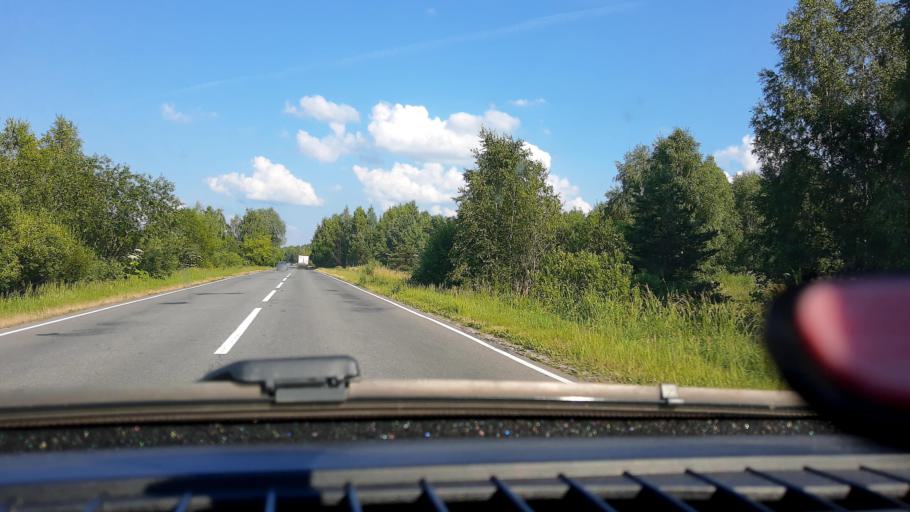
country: RU
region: Nizjnij Novgorod
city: Neklyudovo
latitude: 56.5231
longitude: 43.8720
